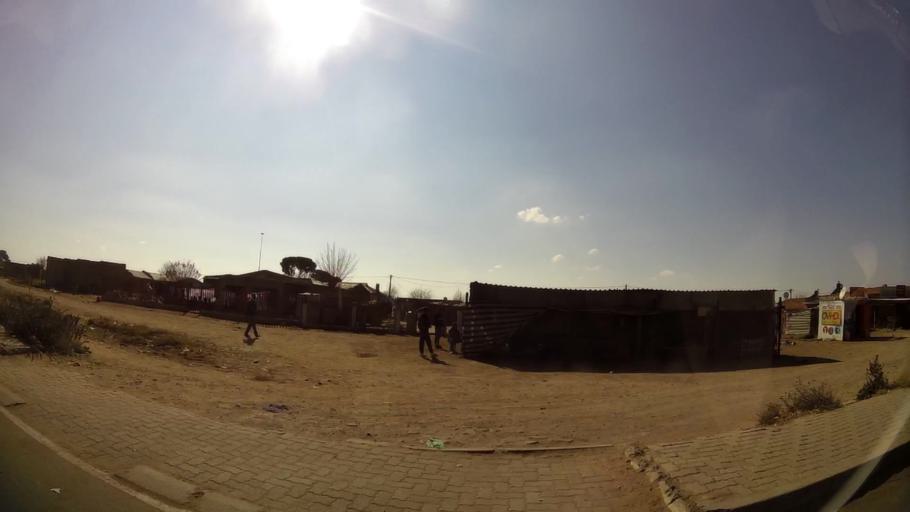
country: ZA
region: Orange Free State
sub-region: Mangaung Metropolitan Municipality
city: Bloemfontein
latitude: -29.1645
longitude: 26.2819
